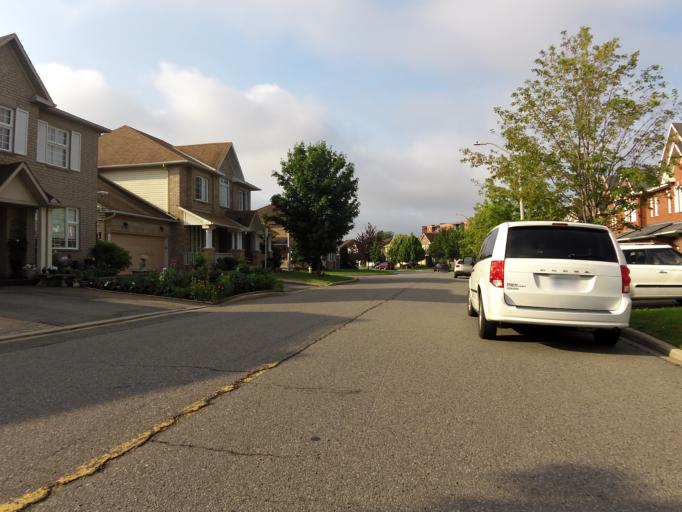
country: CA
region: Ontario
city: Ottawa
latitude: 45.3509
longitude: -75.6682
